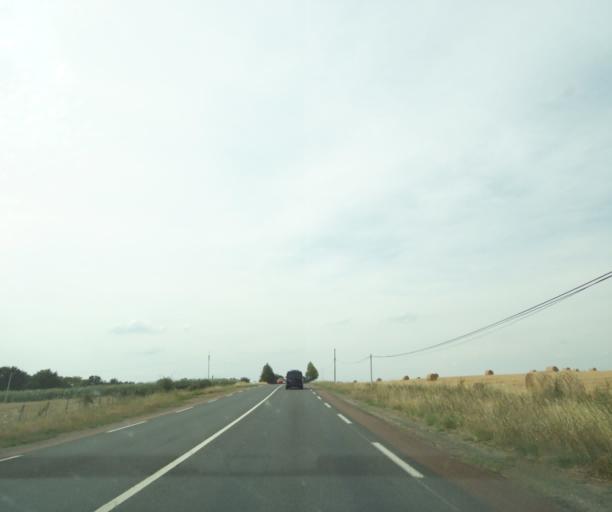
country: FR
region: Pays de la Loire
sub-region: Departement de la Sarthe
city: Luceau
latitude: 47.7235
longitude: 0.3984
